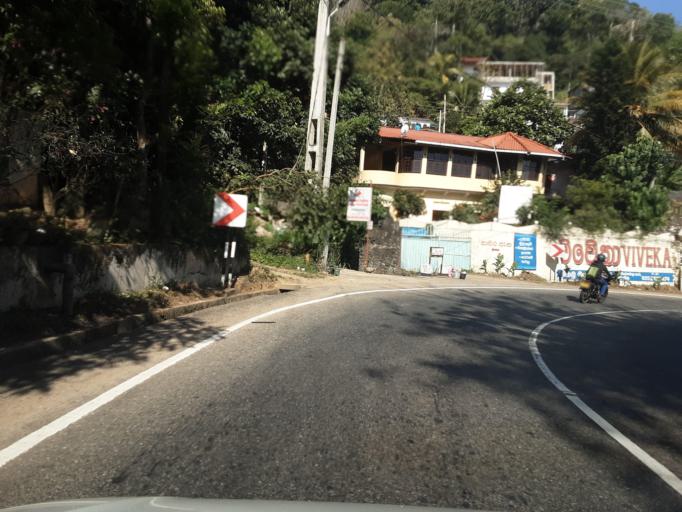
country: LK
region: Uva
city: Badulla
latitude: 6.9841
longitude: 81.0451
